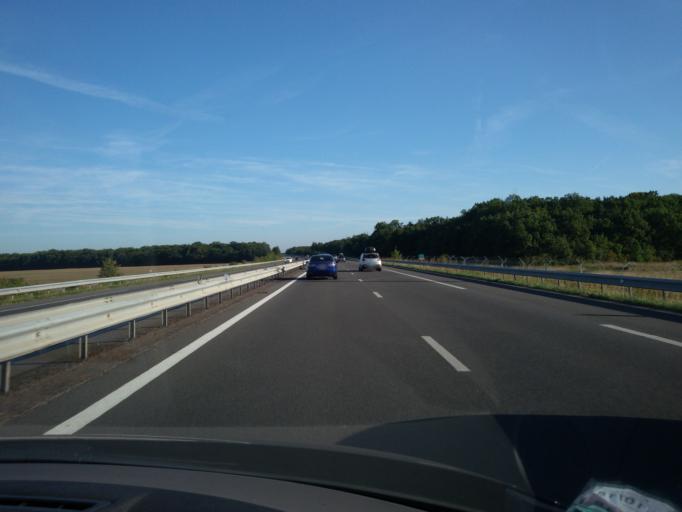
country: FR
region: Centre
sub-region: Departement du Cher
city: Levet
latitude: 46.8669
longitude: 2.4270
